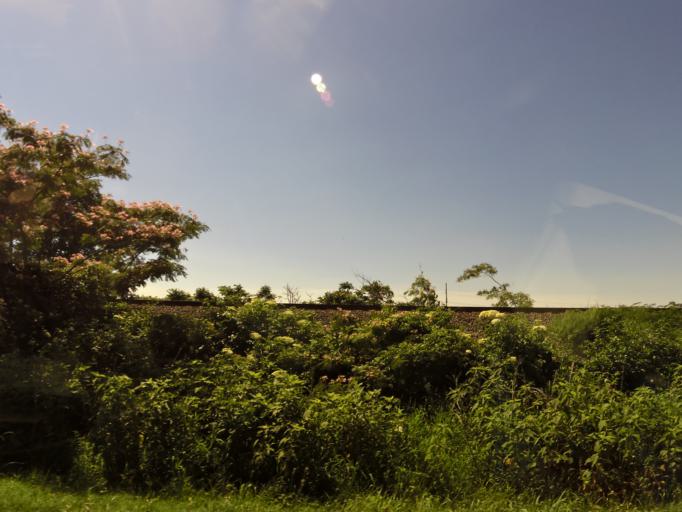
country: US
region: Missouri
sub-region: Dunklin County
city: Campbell
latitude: 36.4624
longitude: -90.1264
